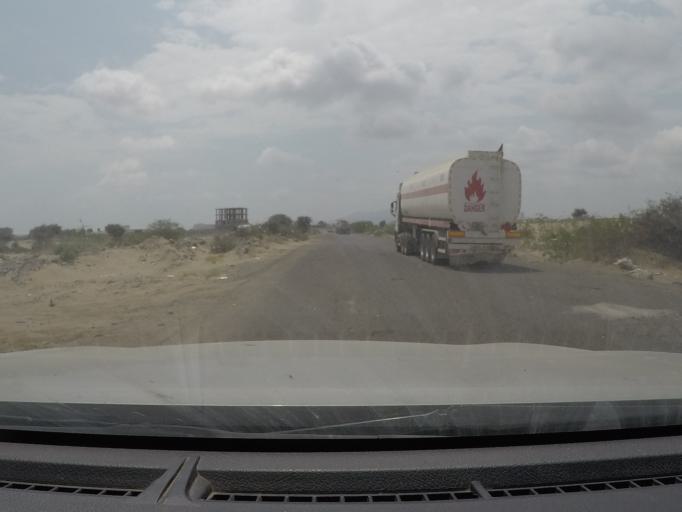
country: YE
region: Aden
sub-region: Ash Shaikh Outhman
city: Ash Shaykh `Uthman
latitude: 12.9085
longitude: 45.0101
